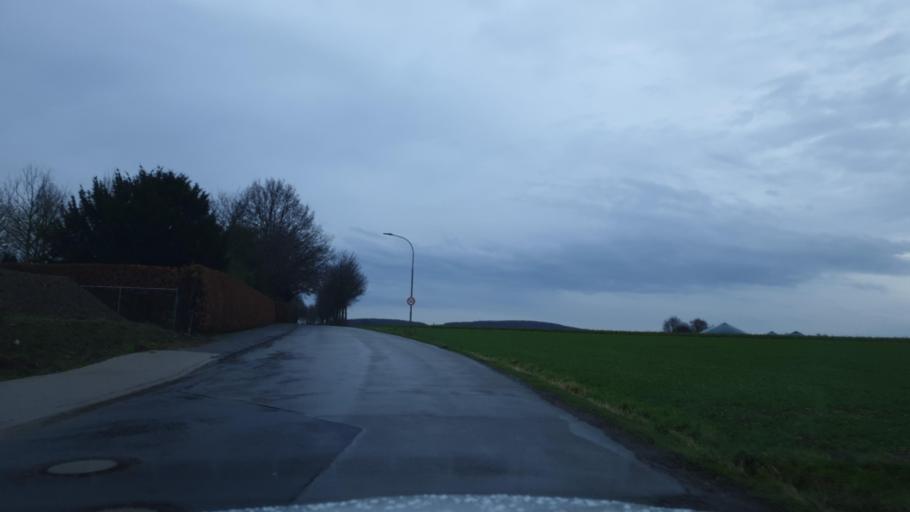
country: DE
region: North Rhine-Westphalia
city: Bad Oeynhausen
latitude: 52.2057
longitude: 8.8295
